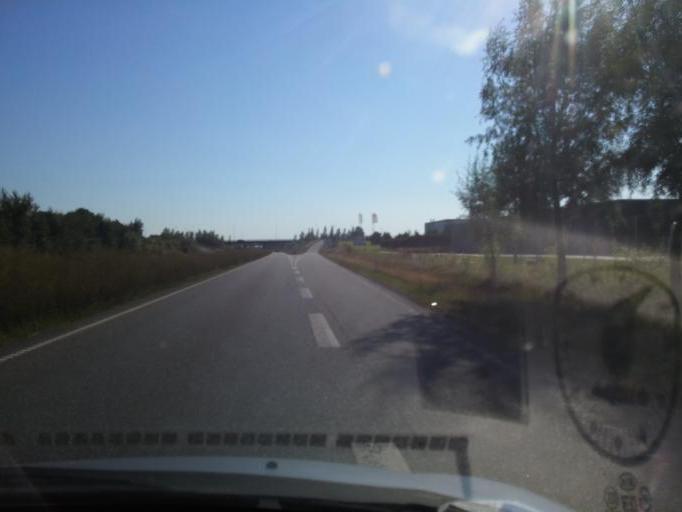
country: DK
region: South Denmark
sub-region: Odense Kommune
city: Neder Holluf
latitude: 55.3652
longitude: 10.4684
